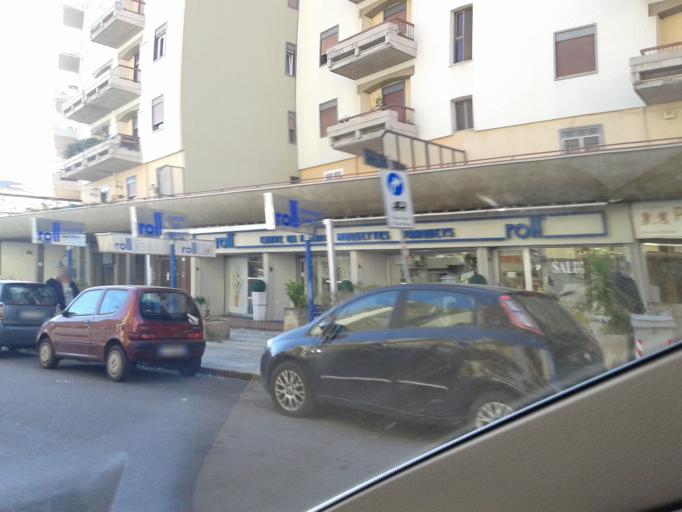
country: IT
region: Sicily
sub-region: Palermo
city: Palermo
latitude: 38.1293
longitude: 13.3390
